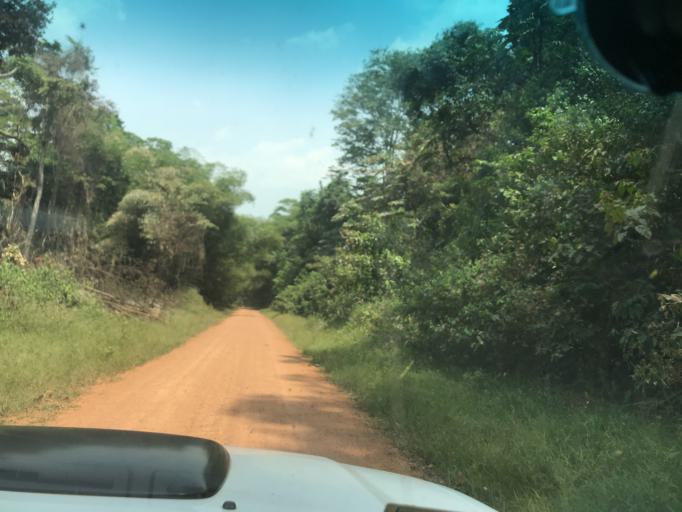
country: CD
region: Eastern Province
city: Aketi
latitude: 2.4905
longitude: 23.2934
